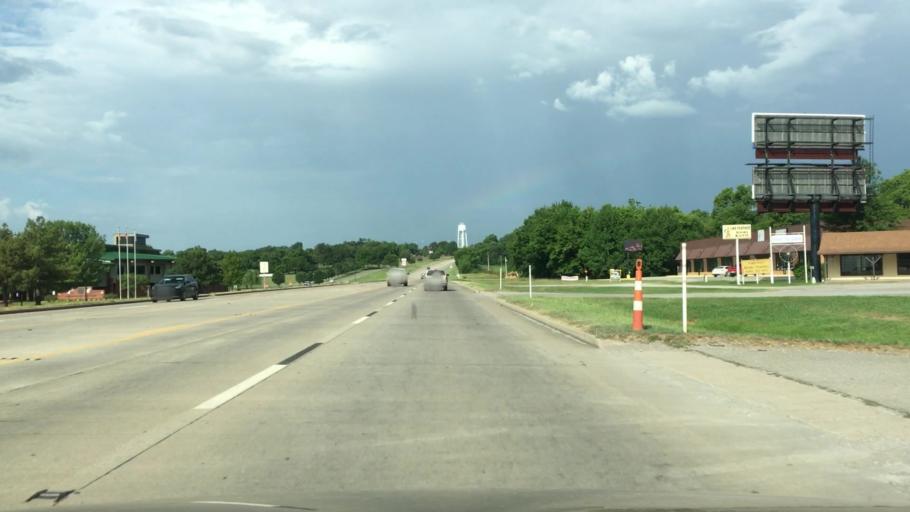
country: US
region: Oklahoma
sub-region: Cherokee County
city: Park Hill
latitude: 35.8537
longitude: -94.9898
